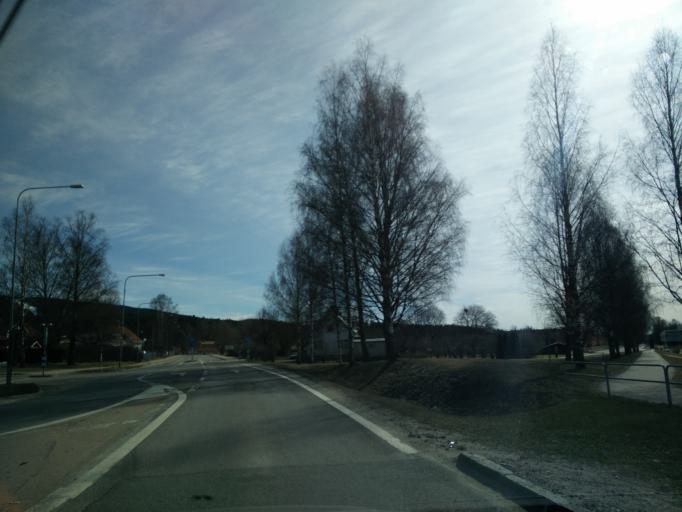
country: SE
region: Vaermland
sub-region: Hagfors Kommun
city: Hagfors
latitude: 60.0389
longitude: 13.7035
